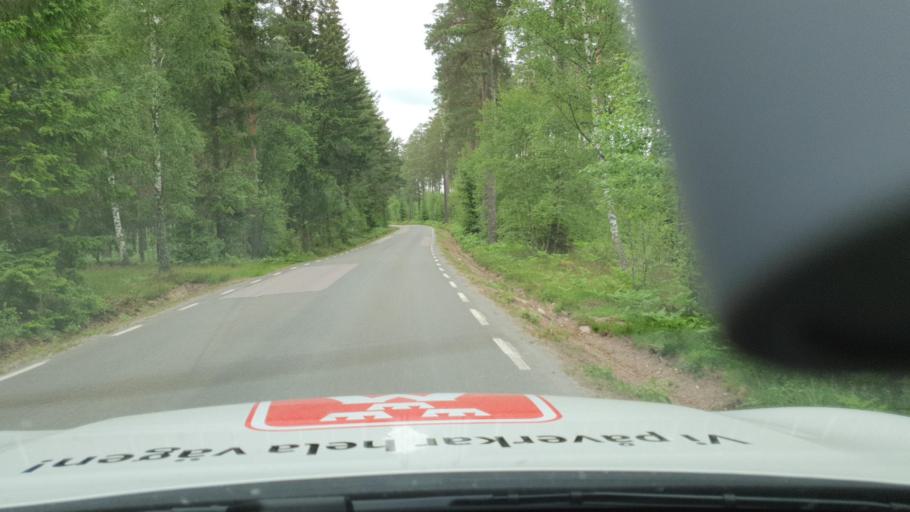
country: SE
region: Vaestra Goetaland
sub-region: Tidaholms Kommun
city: Olofstorp
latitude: 58.2636
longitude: 14.0975
